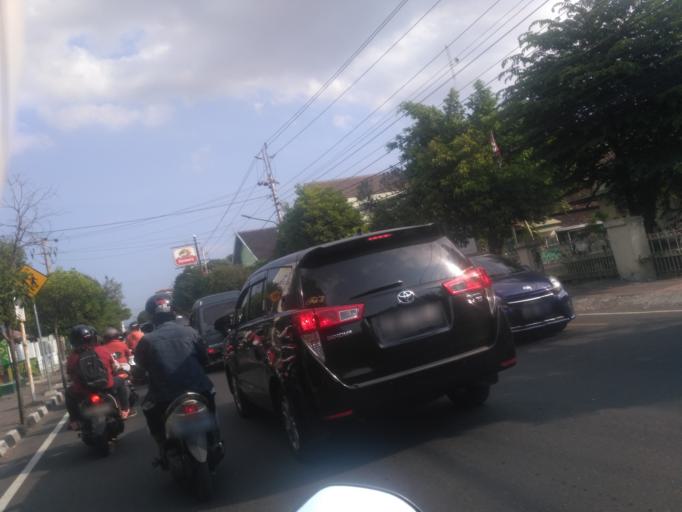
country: ID
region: Daerah Istimewa Yogyakarta
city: Yogyakarta
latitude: -7.7796
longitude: 110.3673
